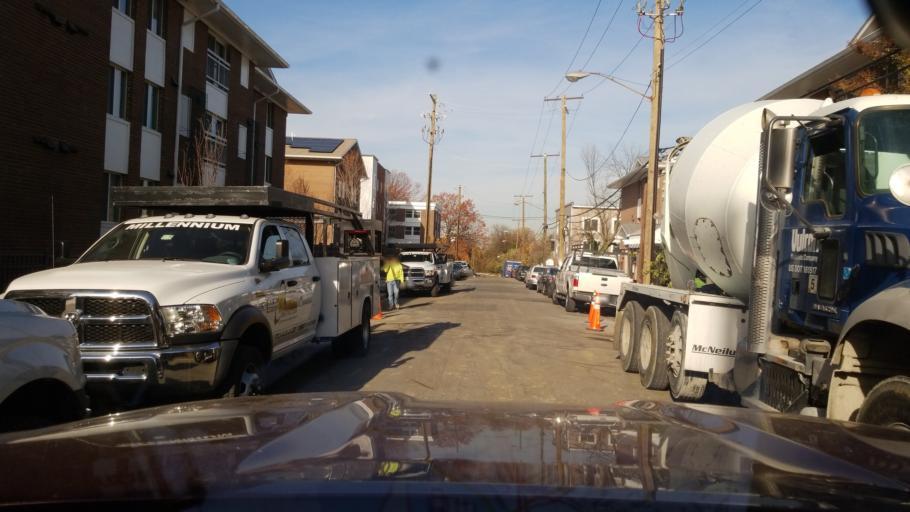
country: US
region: Maryland
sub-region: Prince George's County
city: Hillcrest Heights
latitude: 38.8508
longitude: -76.9867
